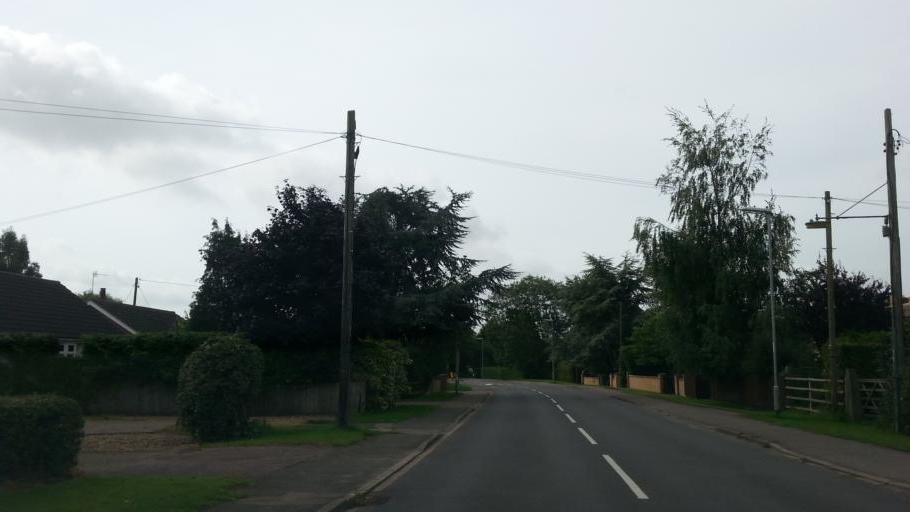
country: GB
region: England
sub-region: Cambridgeshire
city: Comberton
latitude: 52.2098
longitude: -0.0228
